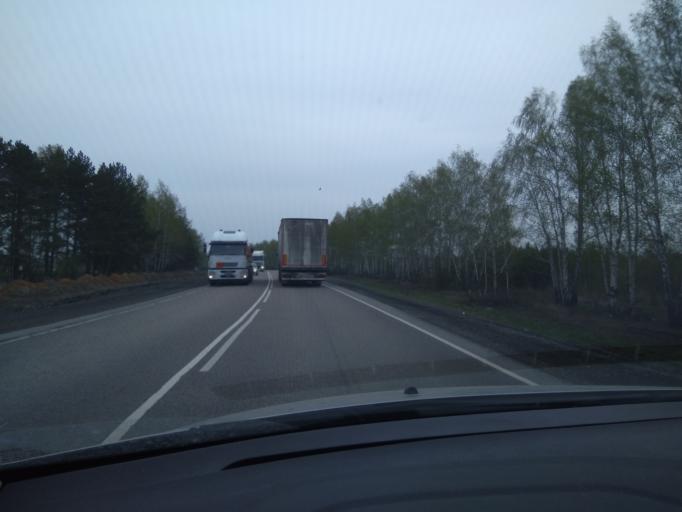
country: RU
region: Sverdlovsk
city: Zarechnyy
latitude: 56.7414
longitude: 61.2677
